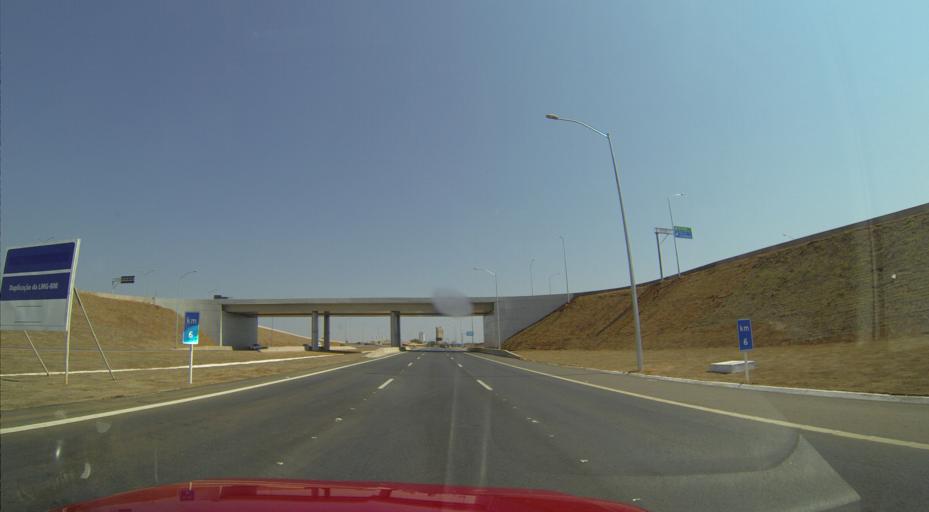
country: BR
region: Minas Gerais
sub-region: Lagoa Santa
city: Lagoa Santa
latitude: -19.6387
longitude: -43.9563
